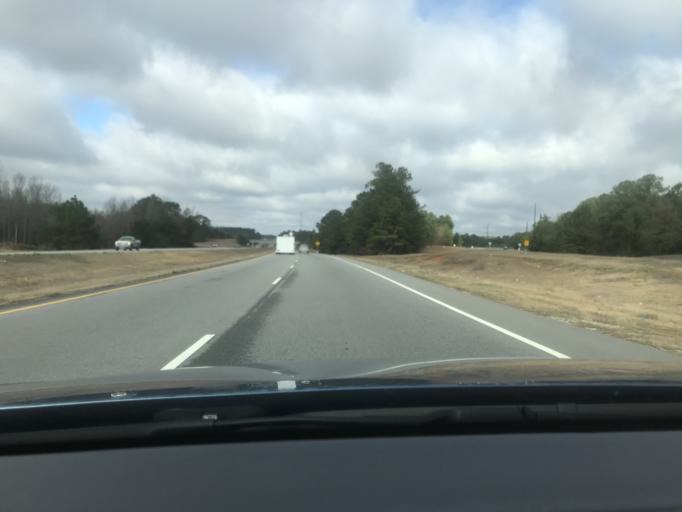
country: US
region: North Carolina
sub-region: Cumberland County
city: Spring Lake
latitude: 35.2669
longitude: -79.0552
